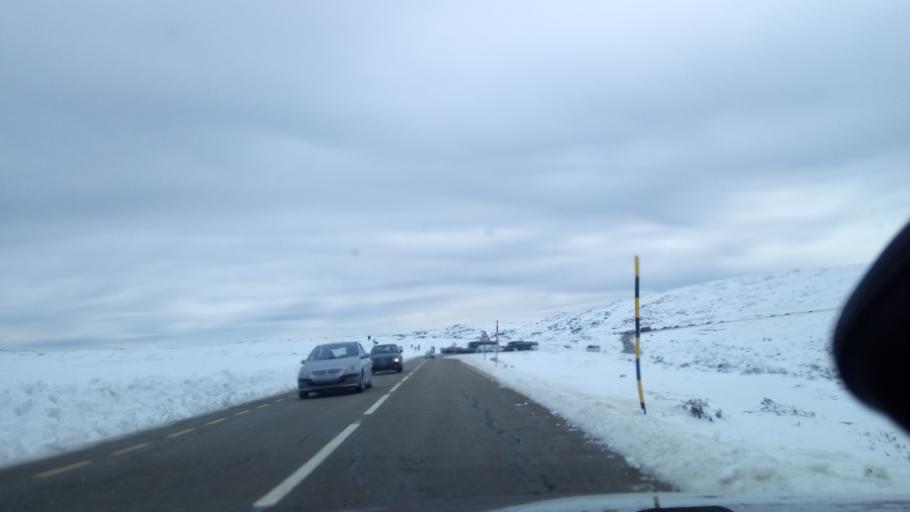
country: PT
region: Guarda
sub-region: Manteigas
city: Manteigas
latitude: 40.3416
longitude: -7.6219
